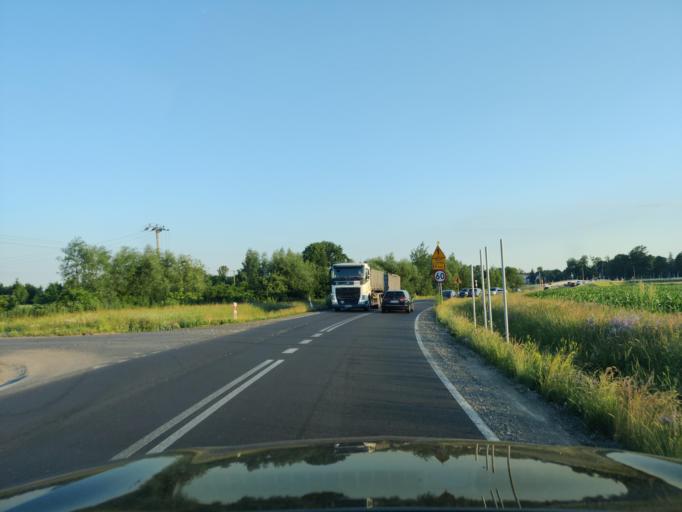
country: PL
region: Masovian Voivodeship
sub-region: Powiat plonski
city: Baboszewo
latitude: 52.7075
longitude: 20.3384
